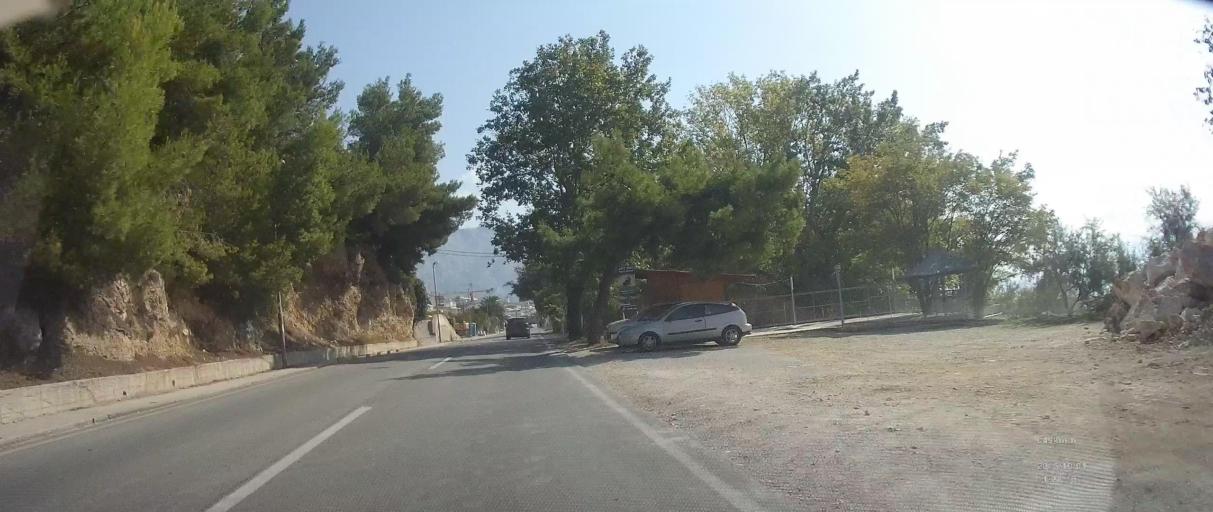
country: HR
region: Splitsko-Dalmatinska
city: Duce
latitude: 43.4414
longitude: 16.6559
